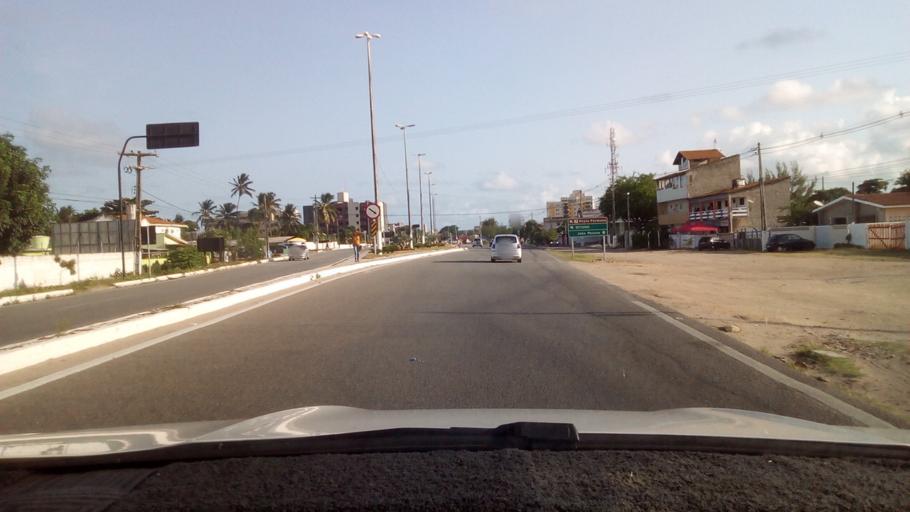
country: BR
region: Paraiba
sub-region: Cabedelo
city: Cabedelo
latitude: -6.9834
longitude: -34.8295
